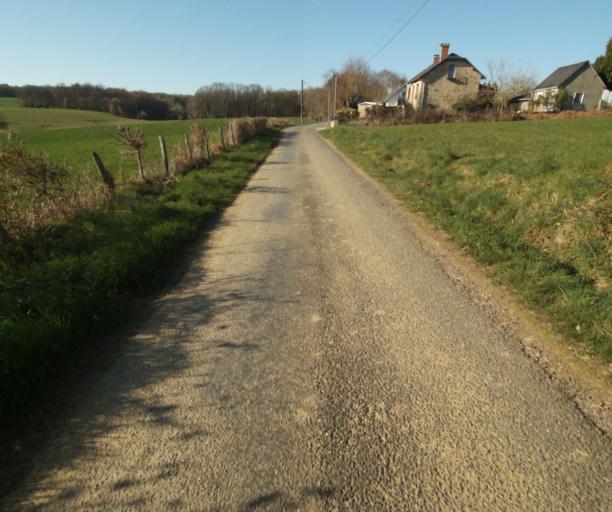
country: FR
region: Limousin
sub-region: Departement de la Correze
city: Chamboulive
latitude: 45.4733
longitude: 1.7244
